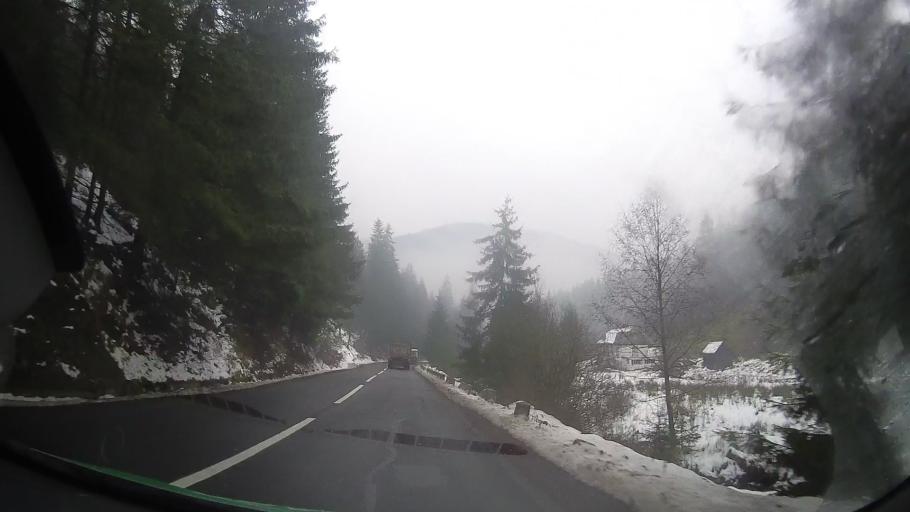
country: RO
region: Harghita
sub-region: Municipiul Gheorgheni
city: Gheorgheni
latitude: 46.7557
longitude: 25.7040
